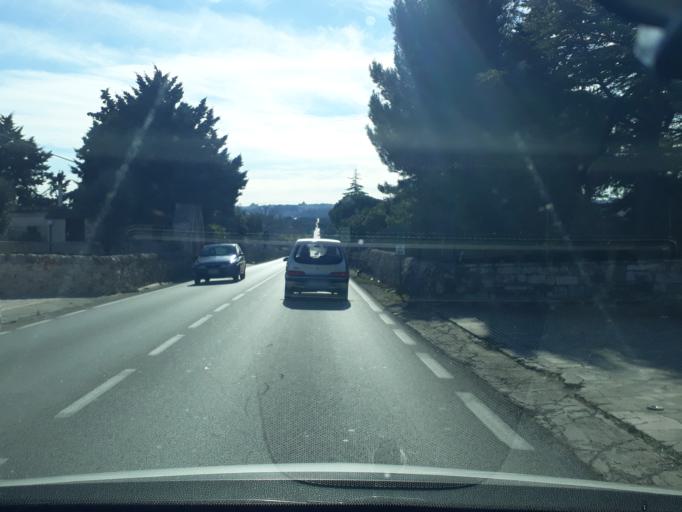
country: IT
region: Apulia
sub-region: Provincia di Bari
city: Locorotondo
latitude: 40.7411
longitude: 17.3325
